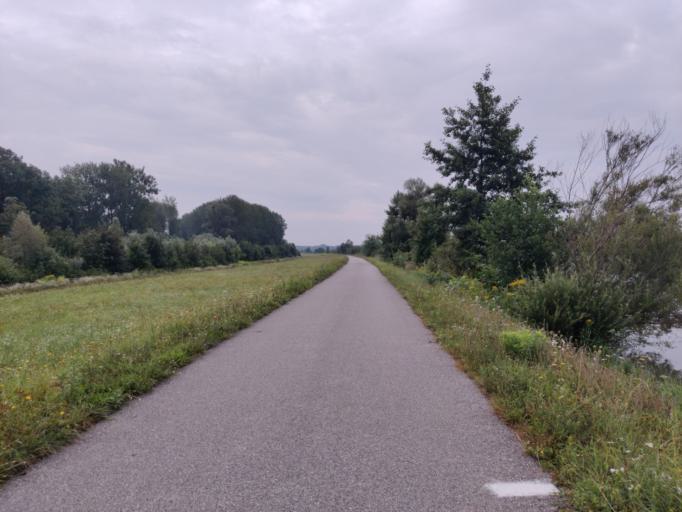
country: AT
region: Upper Austria
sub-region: Politischer Bezirk Urfahr-Umgebung
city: Steyregg
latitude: 48.2654
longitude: 14.3902
